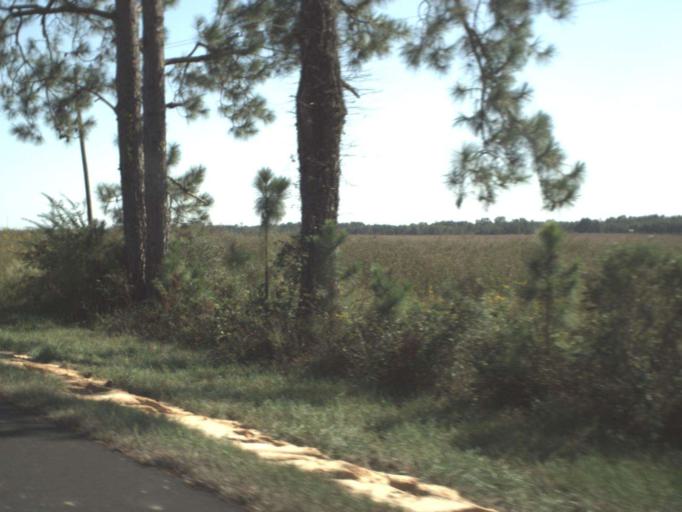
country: US
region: Alabama
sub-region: Covington County
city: Florala
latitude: 30.8816
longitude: -86.2711
